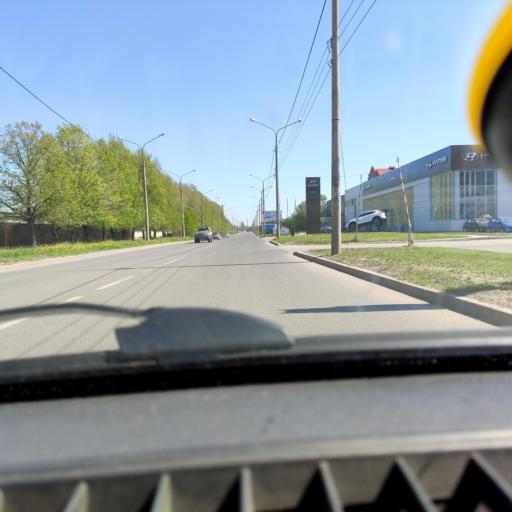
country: RU
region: Samara
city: Tol'yatti
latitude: 53.5410
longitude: 49.4112
